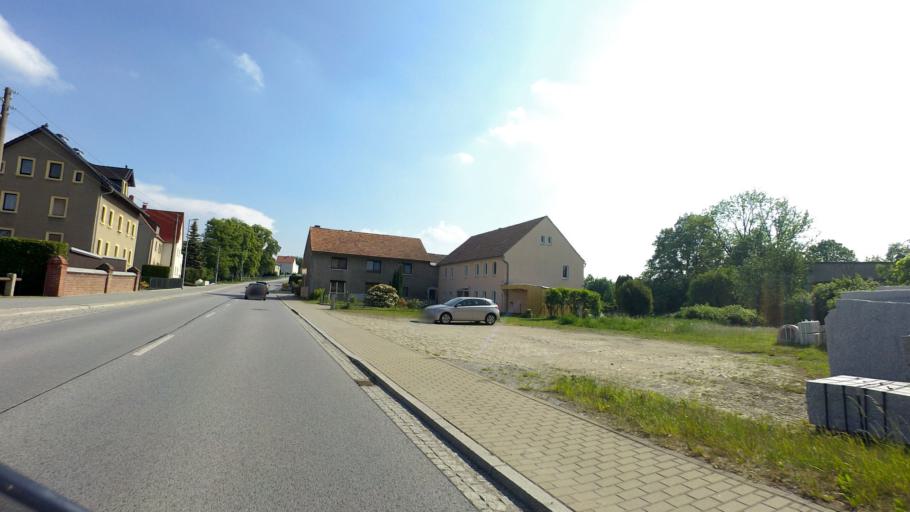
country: DE
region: Saxony
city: Grosspostwitz
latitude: 51.1396
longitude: 14.4415
